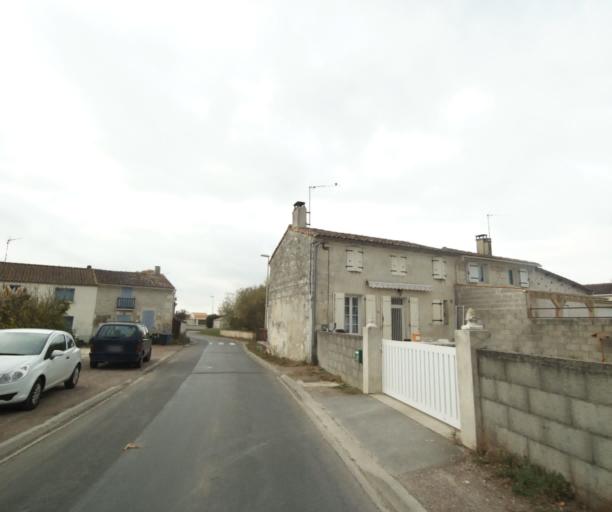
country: FR
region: Poitou-Charentes
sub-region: Departement de la Charente-Maritime
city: Saint-Georges-des-Coteaux
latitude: 45.7720
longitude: -0.7228
